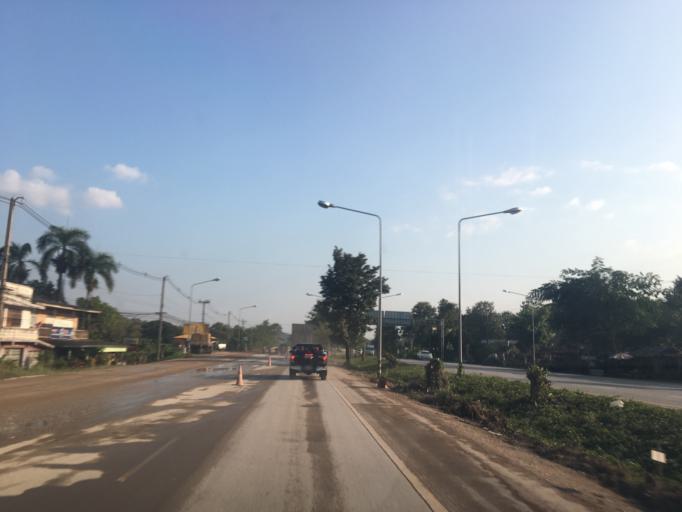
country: TH
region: Lampang
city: Ngao
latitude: 18.7457
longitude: 99.9736
